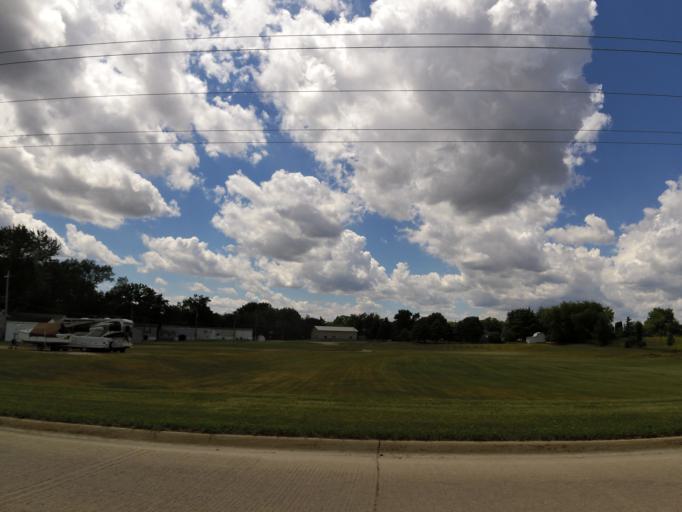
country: US
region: Iowa
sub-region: Fayette County
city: Oelwein
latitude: 42.6455
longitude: -91.9092
